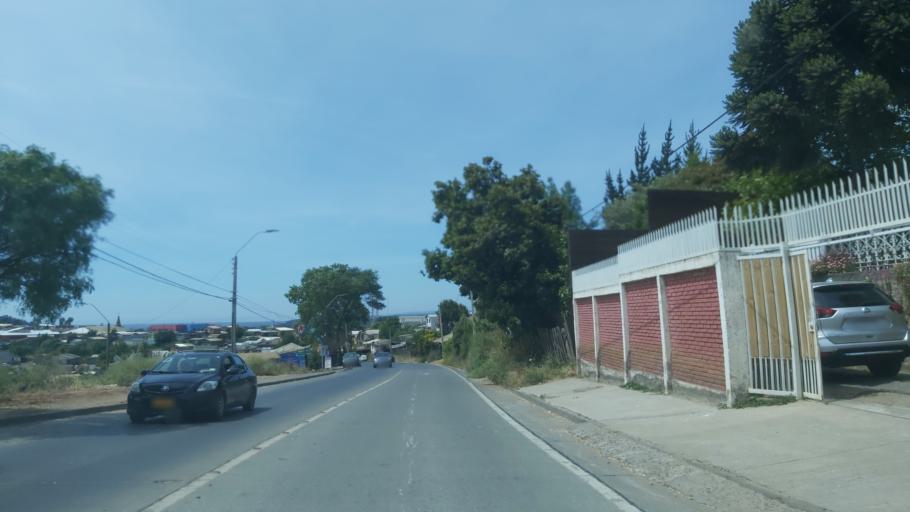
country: CL
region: Maule
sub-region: Provincia de Talca
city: Constitucion
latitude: -35.3447
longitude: -72.4185
